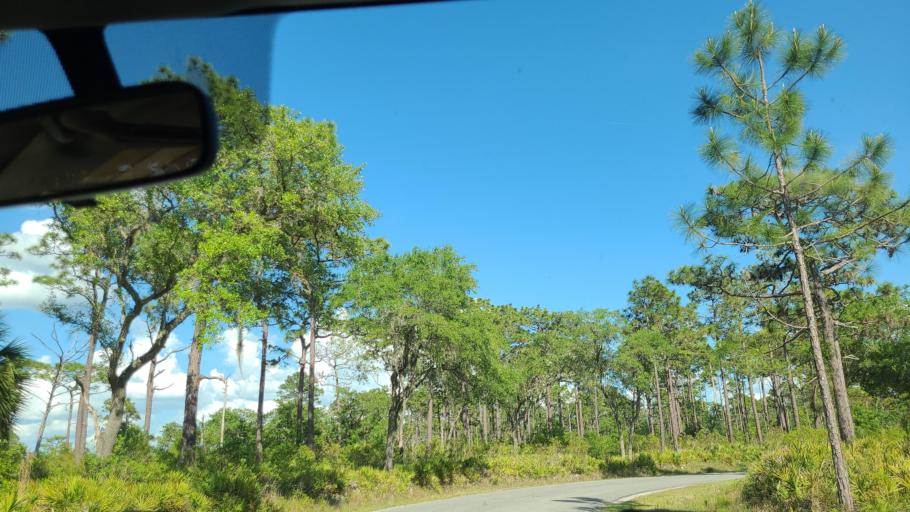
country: US
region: Florida
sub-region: Polk County
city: Babson Park
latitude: 27.9545
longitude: -81.3744
